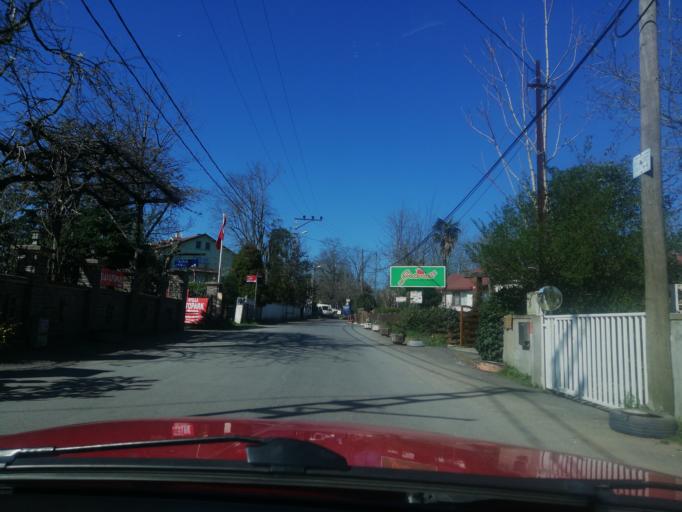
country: TR
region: Istanbul
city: Mahmut Sevket Pasa
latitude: 41.1132
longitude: 29.2116
